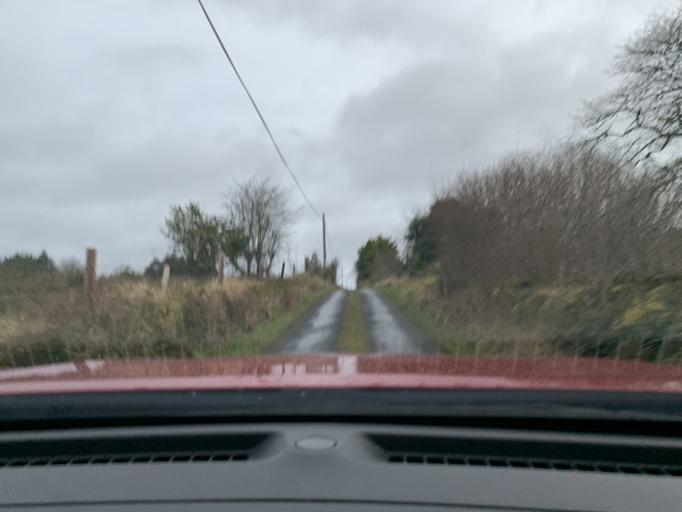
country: IE
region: Connaught
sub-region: Roscommon
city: Boyle
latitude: 53.9850
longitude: -8.3083
